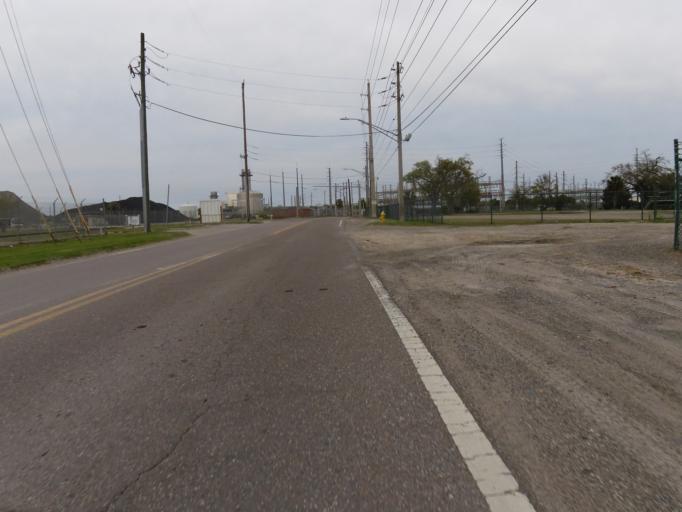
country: US
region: Florida
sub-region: Duval County
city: Jacksonville
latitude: 30.3646
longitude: -81.6296
